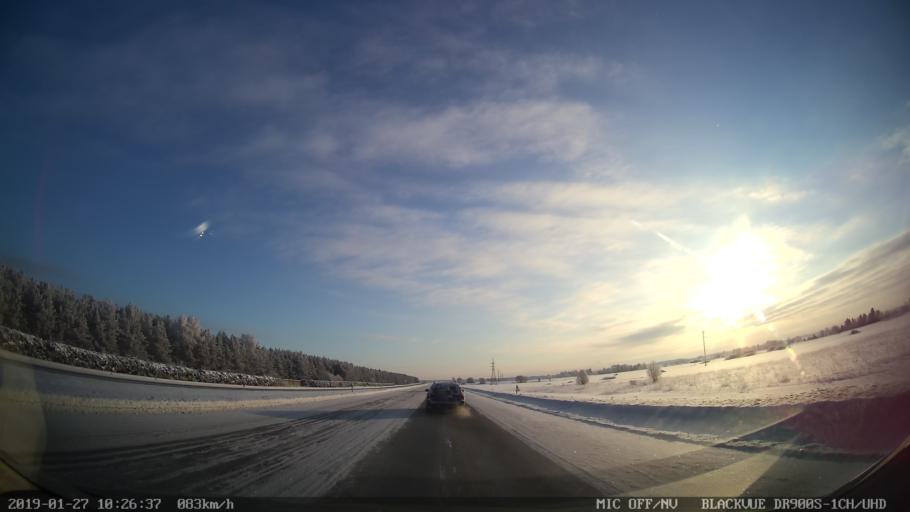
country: EE
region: Harju
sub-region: Maardu linn
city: Maardu
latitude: 59.4459
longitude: 25.1000
